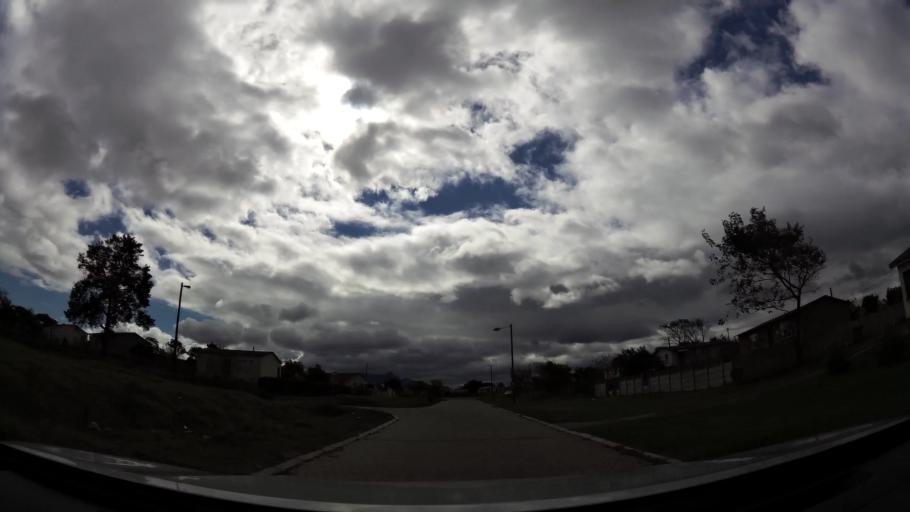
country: ZA
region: Western Cape
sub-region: Eden District Municipality
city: George
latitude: -34.0262
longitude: 22.4662
